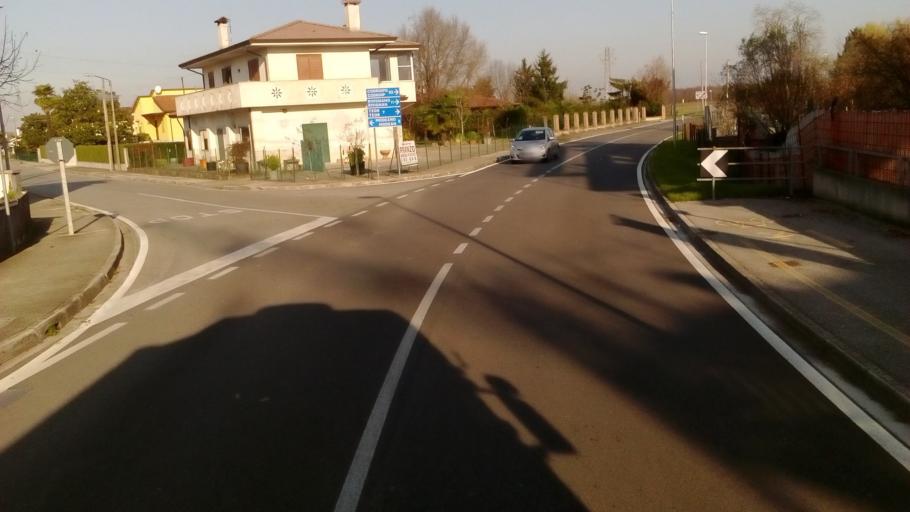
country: IT
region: Friuli Venezia Giulia
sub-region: Provincia di Udine
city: Precenicco
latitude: 45.8052
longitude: 13.0714
